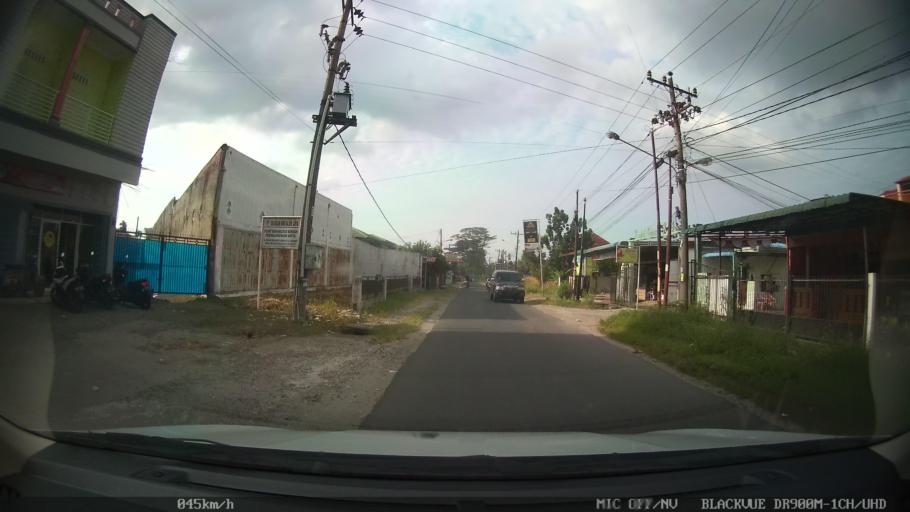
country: ID
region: North Sumatra
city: Sunggal
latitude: 3.5373
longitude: 98.6053
